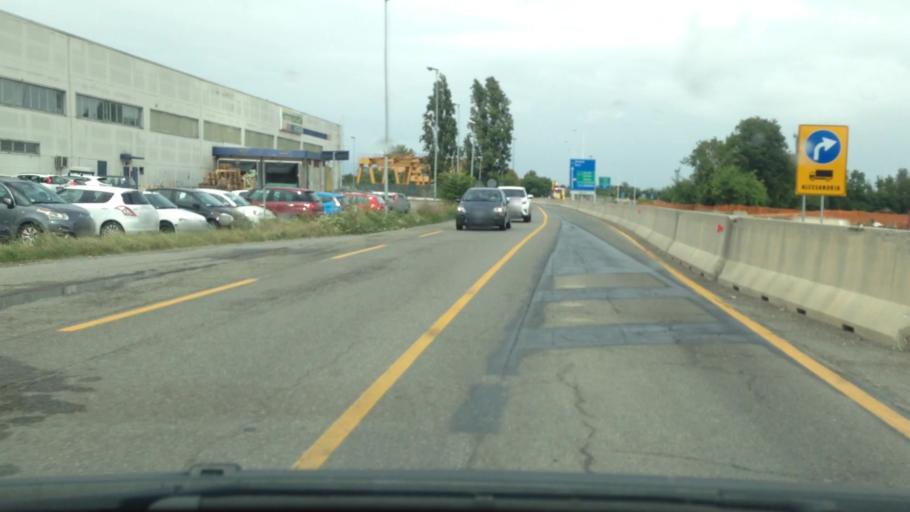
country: IT
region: Piedmont
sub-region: Provincia di Alessandria
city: Tortona
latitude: 44.9027
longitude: 8.8382
